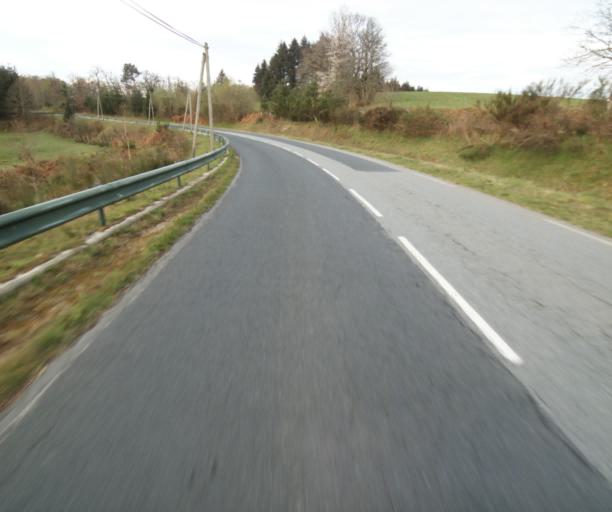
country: FR
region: Limousin
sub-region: Departement de la Correze
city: Correze
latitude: 45.3834
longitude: 1.8647
